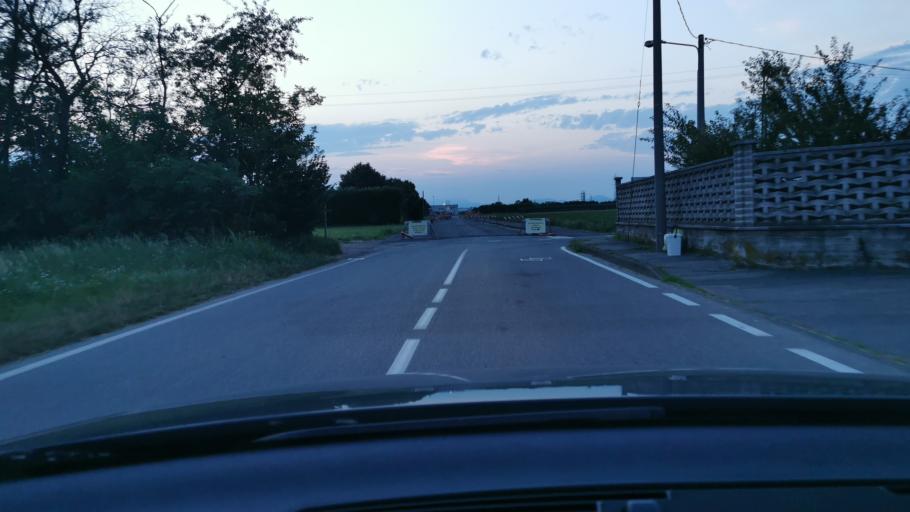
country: IT
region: Lombardy
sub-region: Provincia di Varese
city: Gerenzano
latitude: 45.6406
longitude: 8.9870
